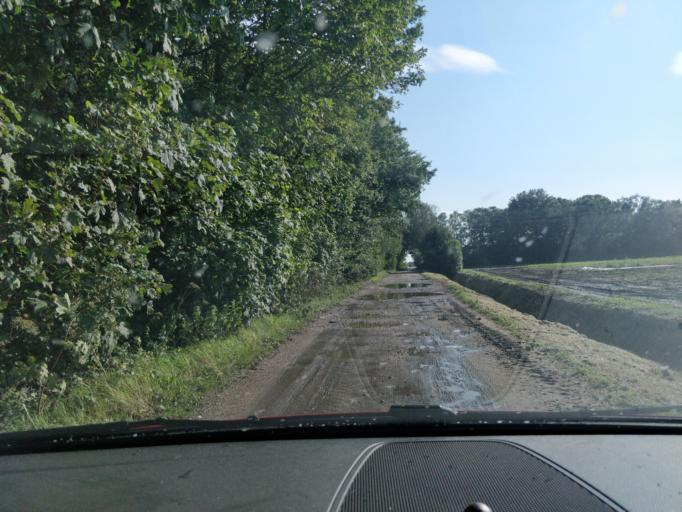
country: GB
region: England
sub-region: Lancashire
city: Banks
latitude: 53.6522
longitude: -2.8997
